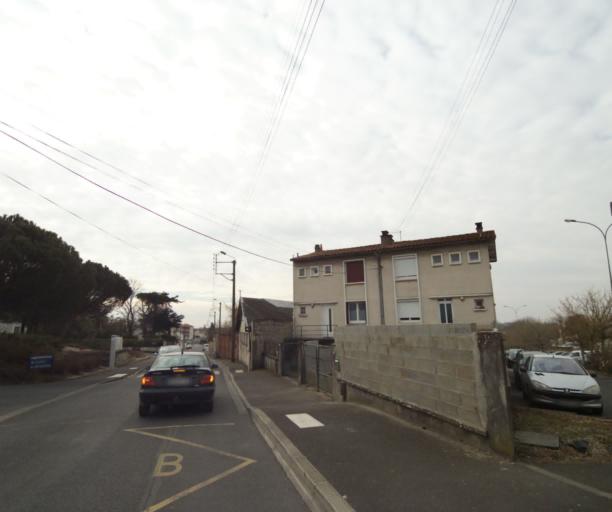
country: FR
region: Poitou-Charentes
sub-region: Departement des Deux-Sevres
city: Niort
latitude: 46.3148
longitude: -0.4537
